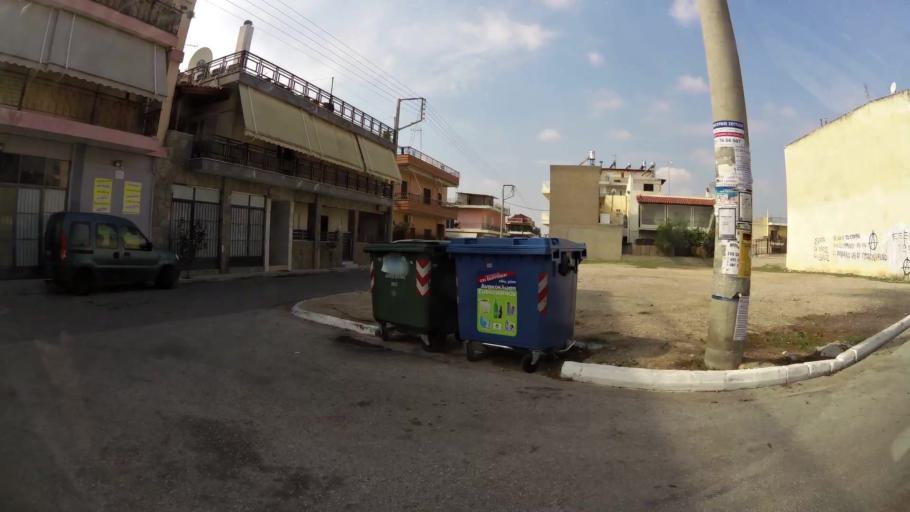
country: GR
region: Attica
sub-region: Nomarchia Dytikis Attikis
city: Zefyri
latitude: 38.0681
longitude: 23.7171
